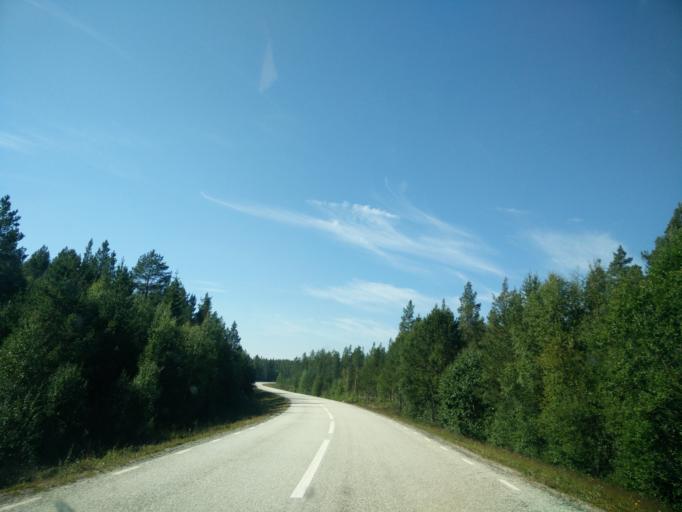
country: SE
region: Jaemtland
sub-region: Are Kommun
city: Jarpen
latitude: 62.8284
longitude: 13.4615
